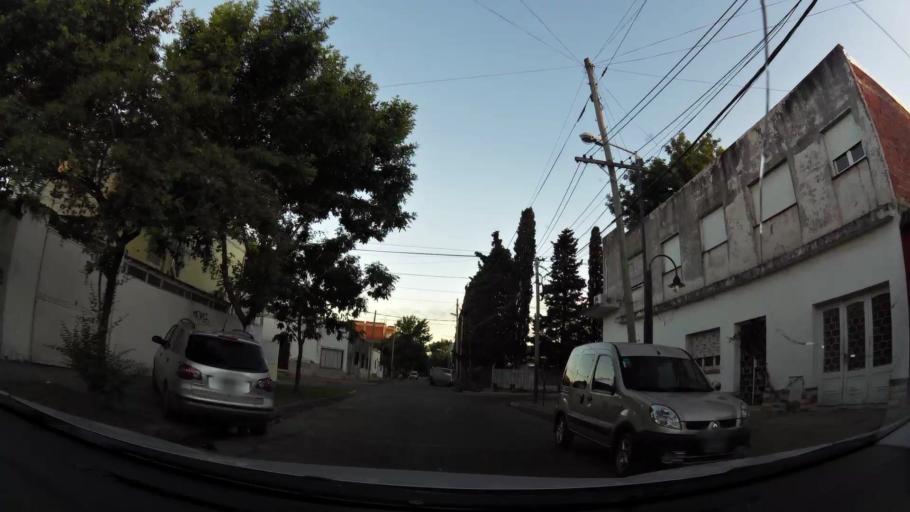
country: AR
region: Buenos Aires
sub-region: Partido de Tigre
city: Tigre
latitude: -34.4431
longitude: -58.5650
